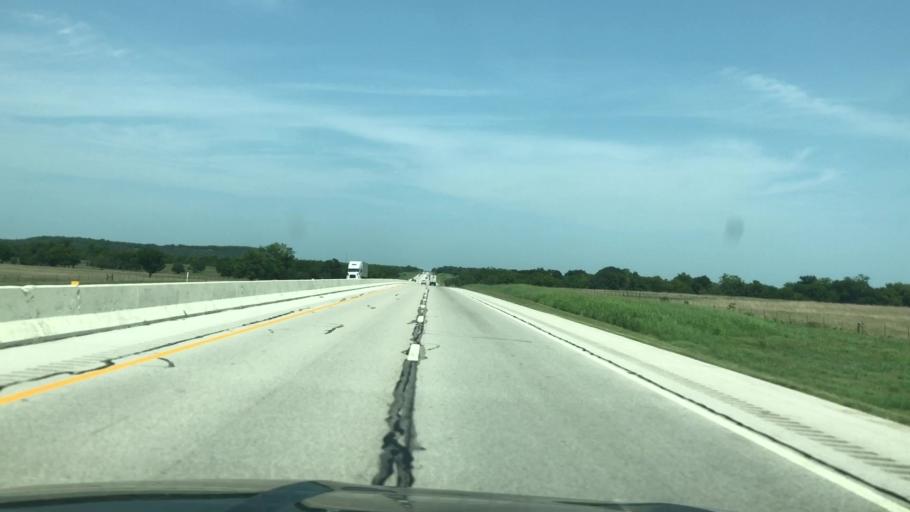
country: US
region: Oklahoma
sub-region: Rogers County
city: Bushyhead
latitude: 36.3684
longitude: -95.4458
